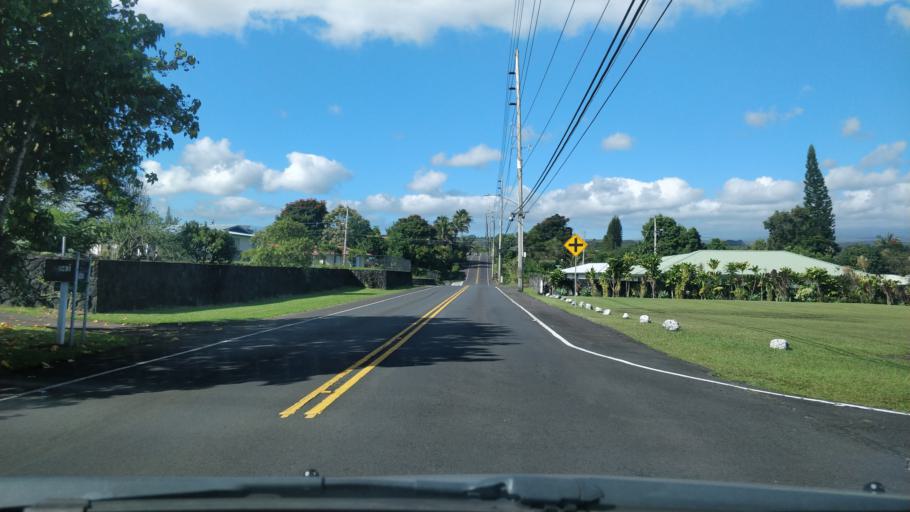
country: US
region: Hawaii
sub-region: Hawaii County
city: Hilo
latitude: 19.6824
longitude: -155.1004
